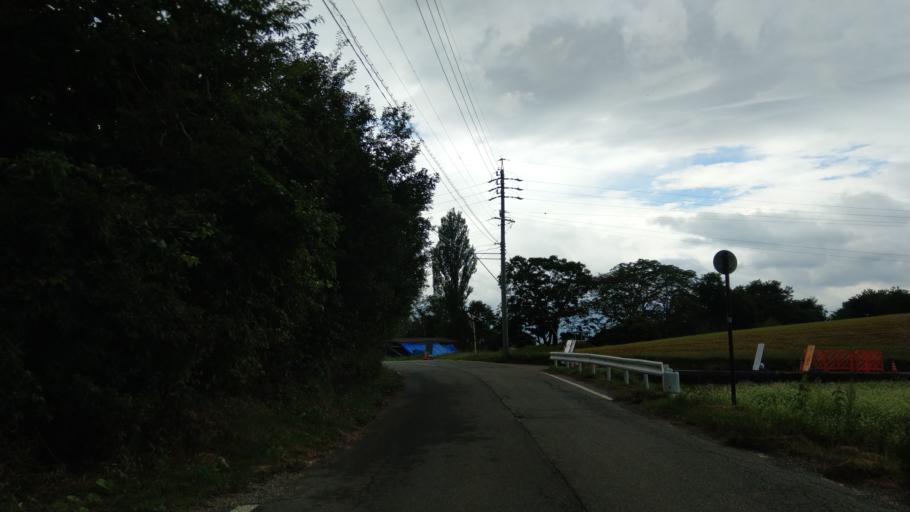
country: JP
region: Nagano
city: Komoro
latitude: 36.3033
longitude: 138.3881
